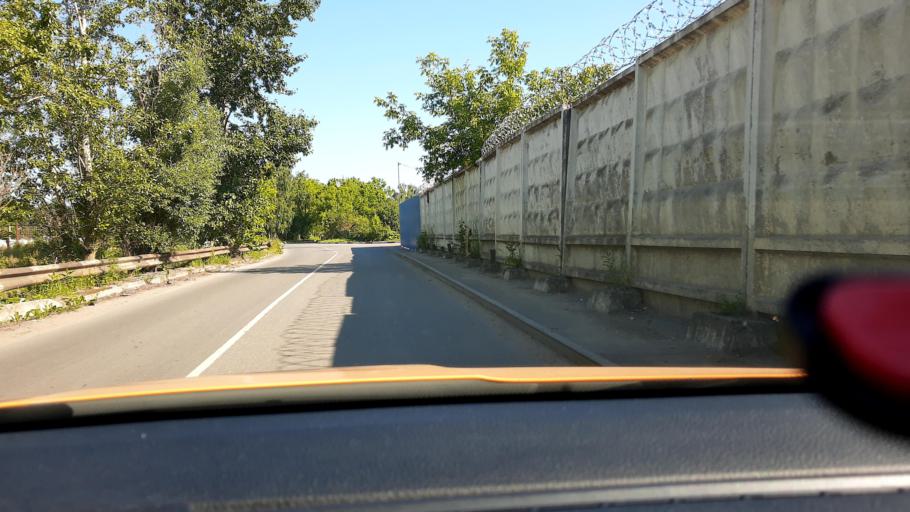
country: RU
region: Moskovskaya
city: Arkhangel'skoye
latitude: 55.7966
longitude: 37.3078
